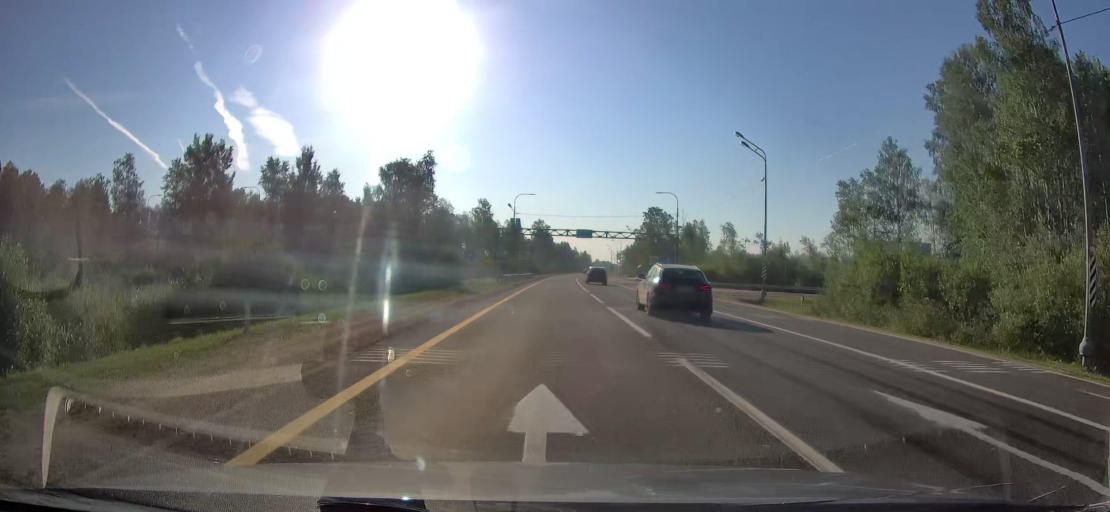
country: RU
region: Leningrad
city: Sinyavino
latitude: 59.9082
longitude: 31.0431
